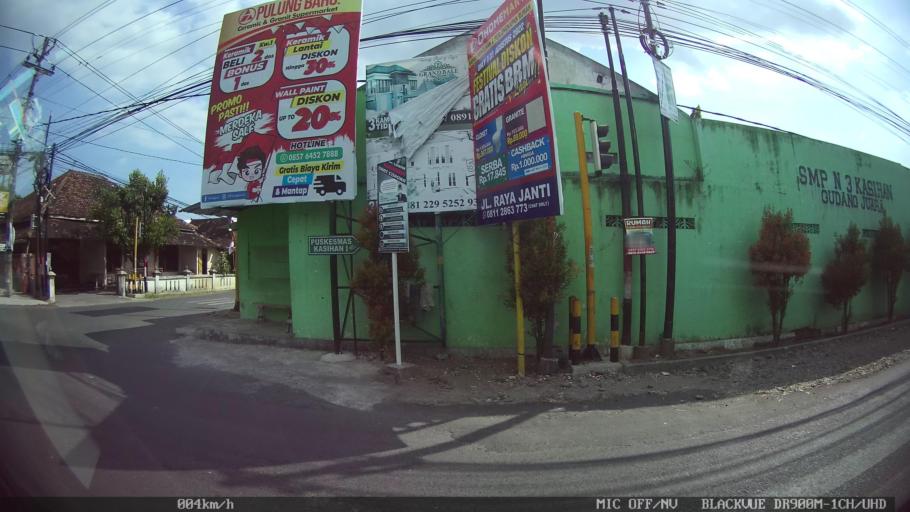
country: ID
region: Daerah Istimewa Yogyakarta
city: Kasihan
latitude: -7.8400
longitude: 110.3131
